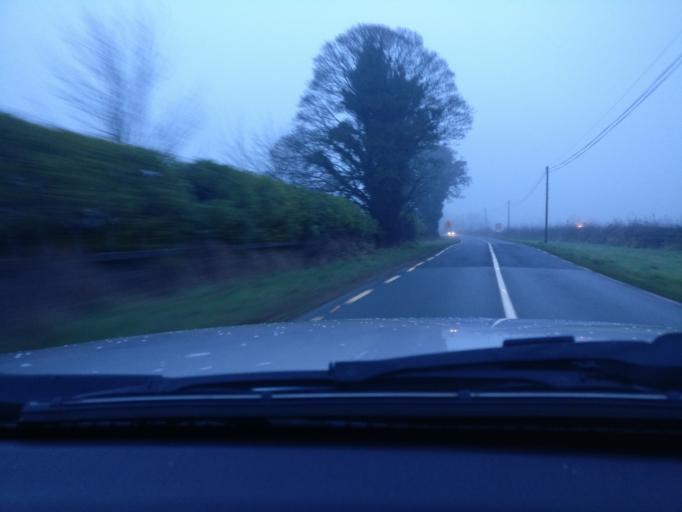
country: IE
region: Leinster
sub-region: An Mhi
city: Athboy
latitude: 53.6090
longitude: -6.9578
